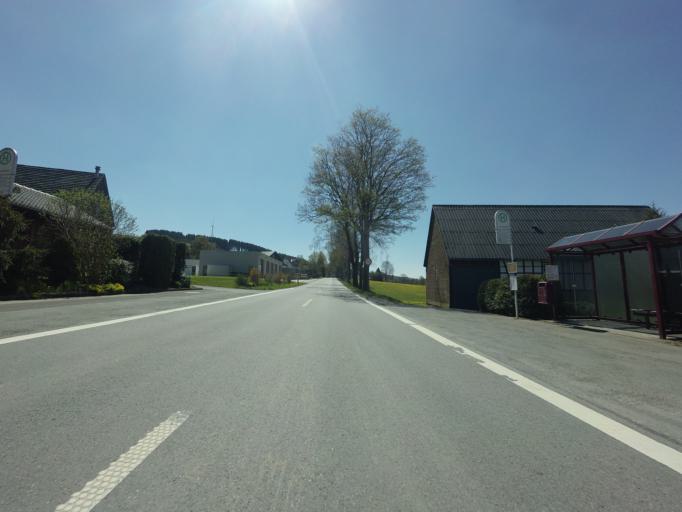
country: DE
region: North Rhine-Westphalia
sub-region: Regierungsbezirk Arnsberg
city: Erndtebruck
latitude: 51.0094
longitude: 8.2608
